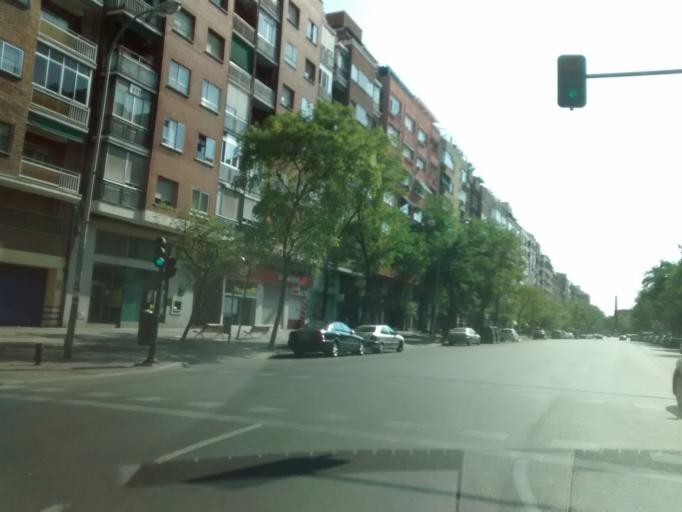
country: ES
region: Madrid
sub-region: Provincia de Madrid
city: Arganzuela
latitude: 40.4010
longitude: -3.6986
